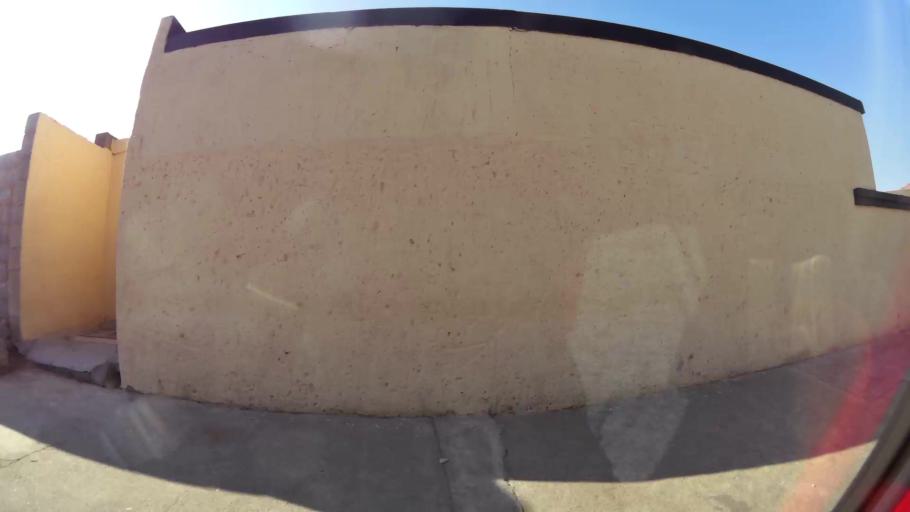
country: ZA
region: Gauteng
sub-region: City of Johannesburg Metropolitan Municipality
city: Soweto
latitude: -26.2479
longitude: 27.9505
